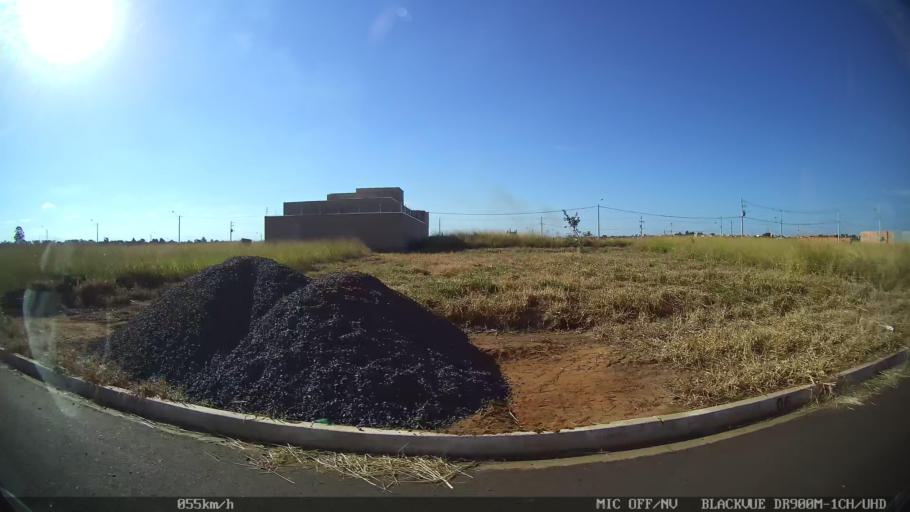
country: BR
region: Sao Paulo
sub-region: Franca
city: Franca
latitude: -20.5064
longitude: -47.4297
